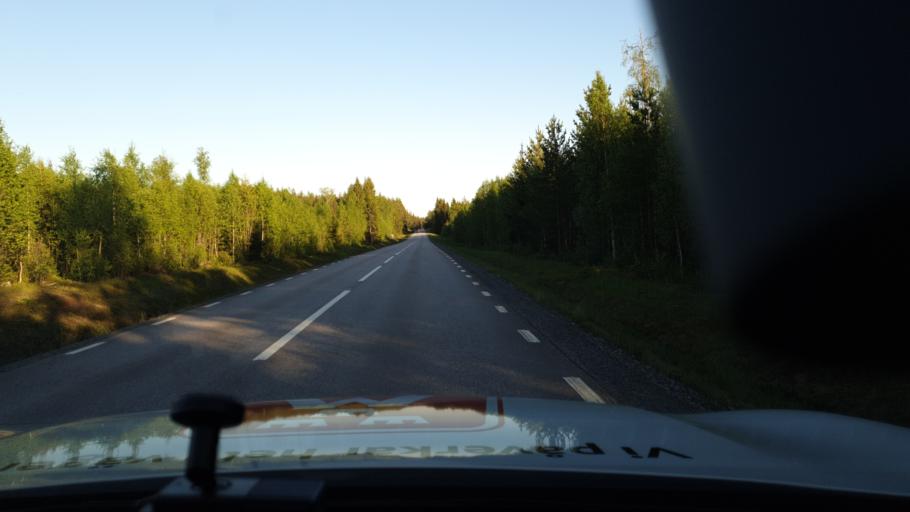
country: SE
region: Vaesterbotten
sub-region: Umea Kommun
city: Ersmark
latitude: 63.9560
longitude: 20.2938
